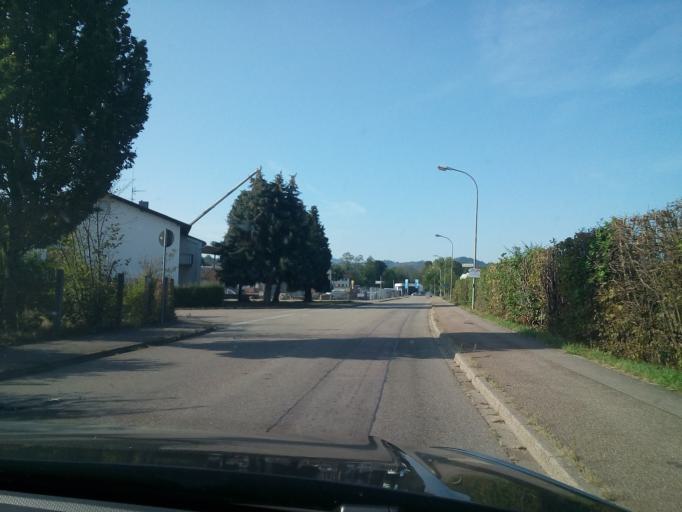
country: DE
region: Baden-Wuerttemberg
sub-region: Freiburg Region
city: Oberkirch
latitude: 48.5392
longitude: 8.0626
